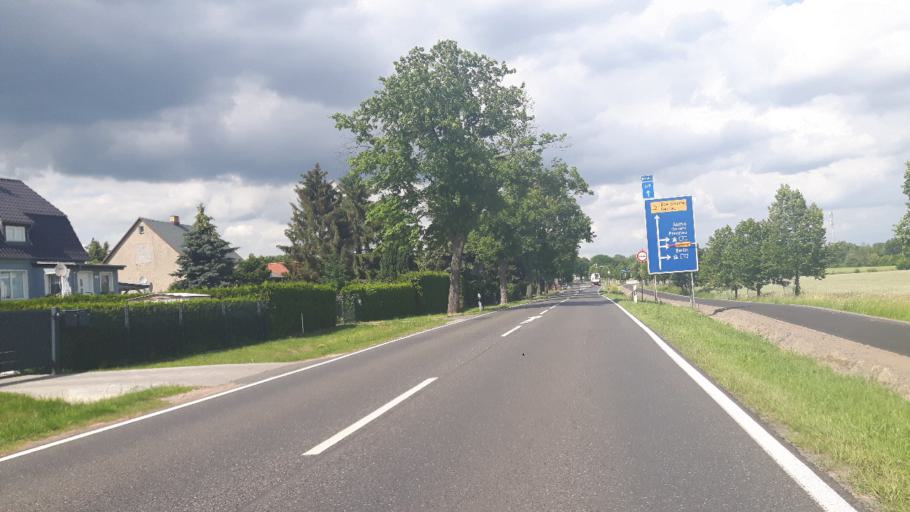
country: DE
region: Brandenburg
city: Bernau bei Berlin
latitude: 52.6425
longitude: 13.5632
